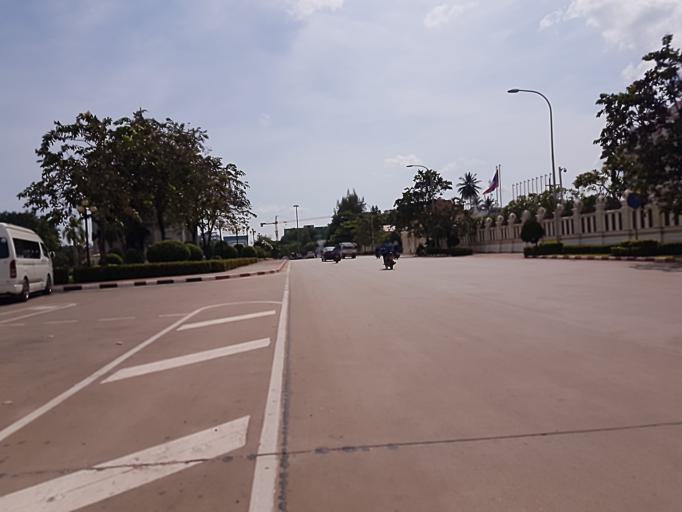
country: LA
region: Vientiane
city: Vientiane
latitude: 17.9719
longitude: 102.6195
